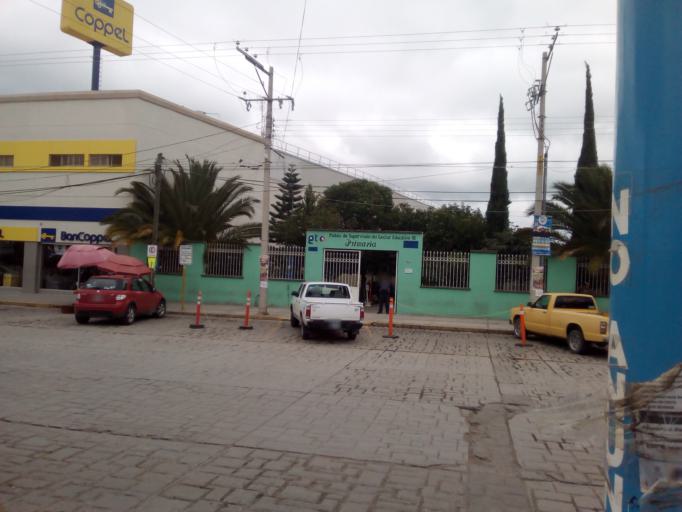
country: MX
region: Guerrero
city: San Luis de la Paz
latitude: 21.2965
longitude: -100.5250
